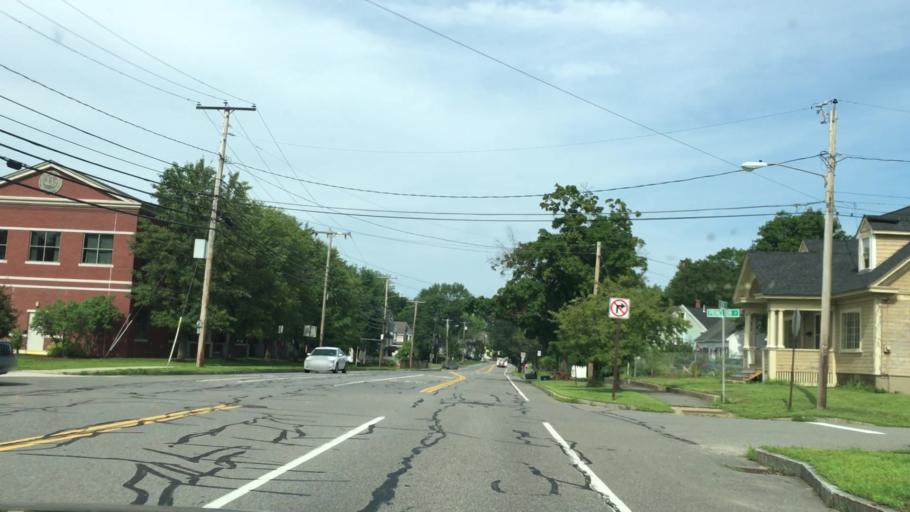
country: US
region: New Hampshire
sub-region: Merrimack County
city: Concord
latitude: 43.1931
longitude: -71.5437
